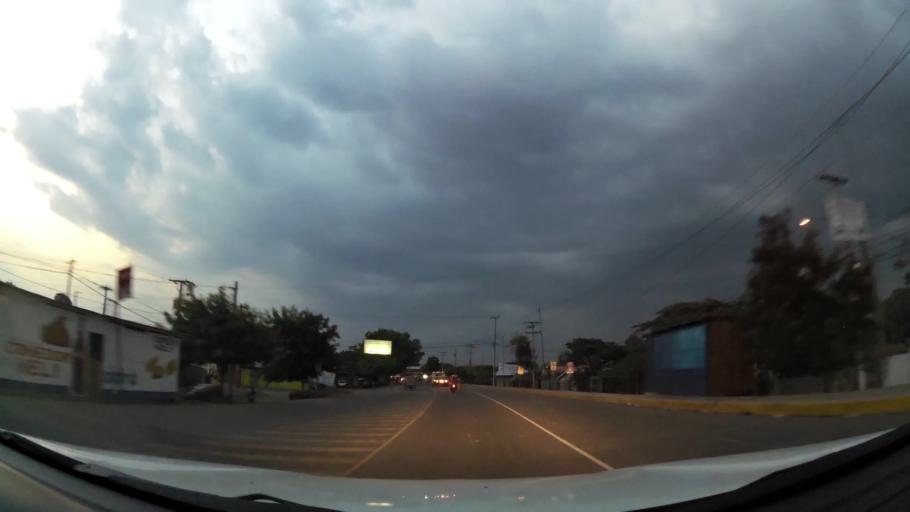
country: NI
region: Matagalpa
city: Ciudad Dario
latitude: 12.8547
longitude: -86.0992
